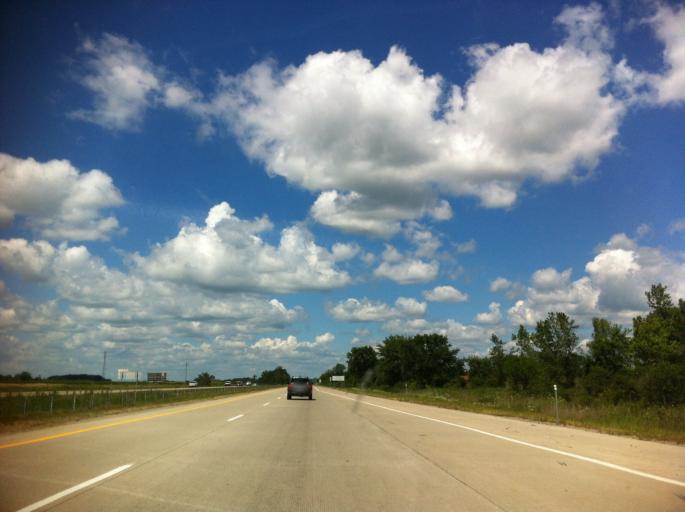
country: US
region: Ohio
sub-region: Lucas County
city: Sylvania
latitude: 41.7733
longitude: -83.6951
